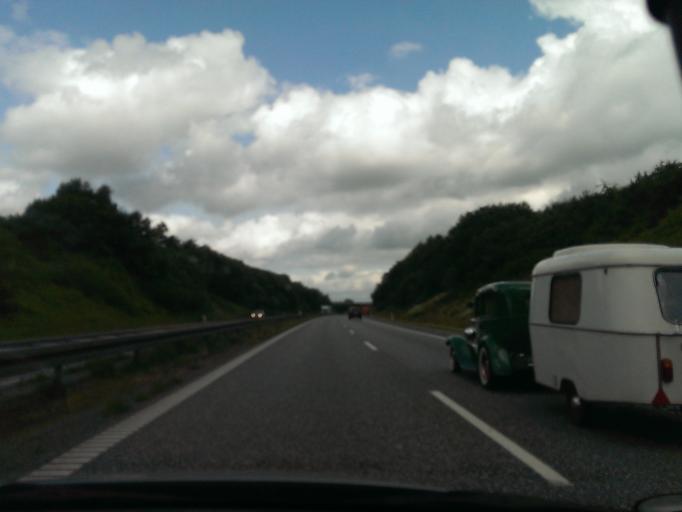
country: DK
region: North Denmark
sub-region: Mariagerfjord Kommune
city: Hobro
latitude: 56.6030
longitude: 9.7504
